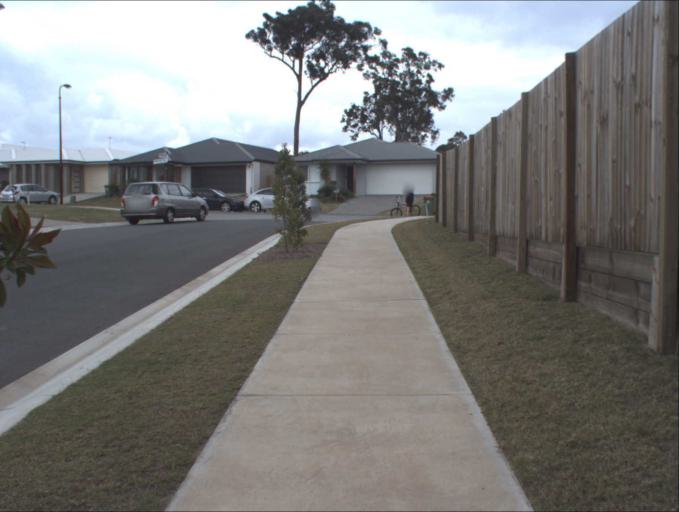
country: AU
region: Queensland
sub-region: Logan
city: Logan Reserve
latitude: -27.7110
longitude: 153.1101
